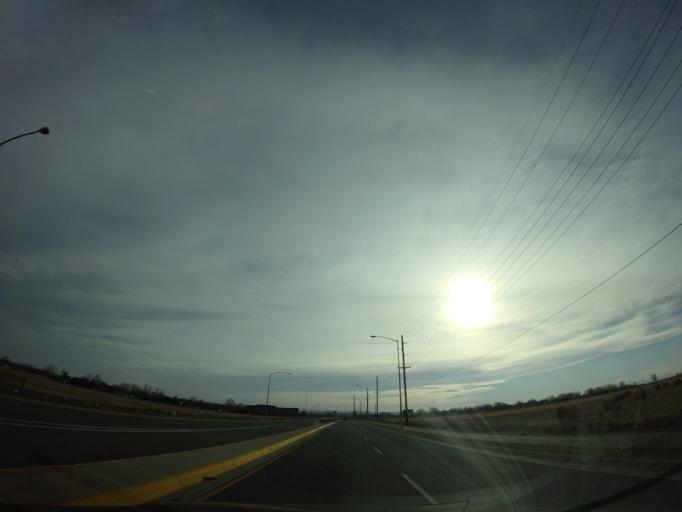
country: US
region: Montana
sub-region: Yellowstone County
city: Billings
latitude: 45.7796
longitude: -108.6176
